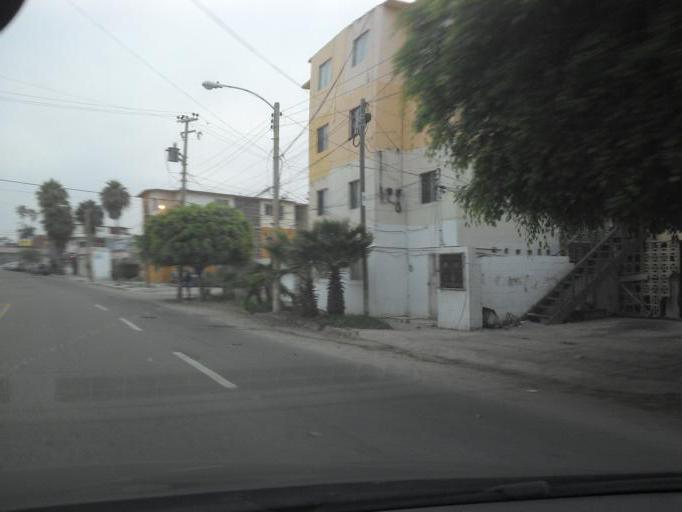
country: MX
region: Baja California
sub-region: Tijuana
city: La Esperanza [Granjas Familiares]
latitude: 32.5097
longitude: -117.1206
